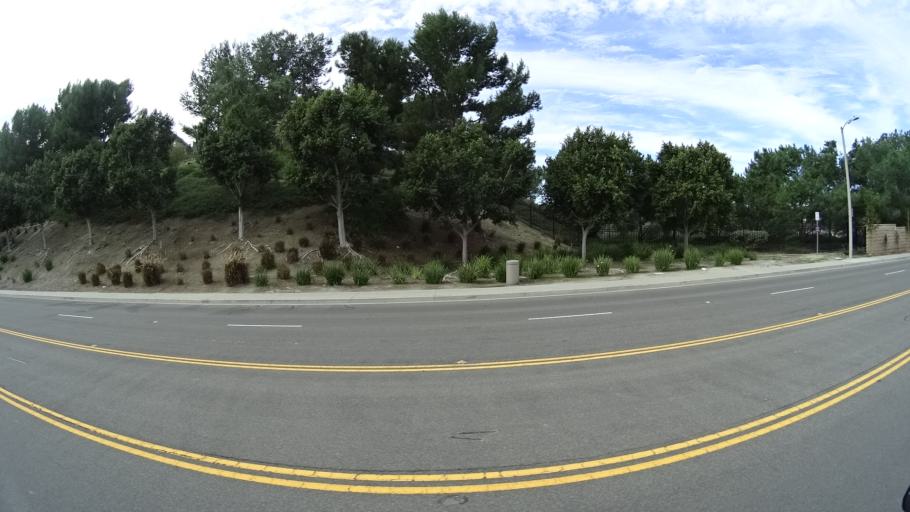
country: US
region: California
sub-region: Orange County
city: Aliso Viejo
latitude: 33.5614
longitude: -117.7302
